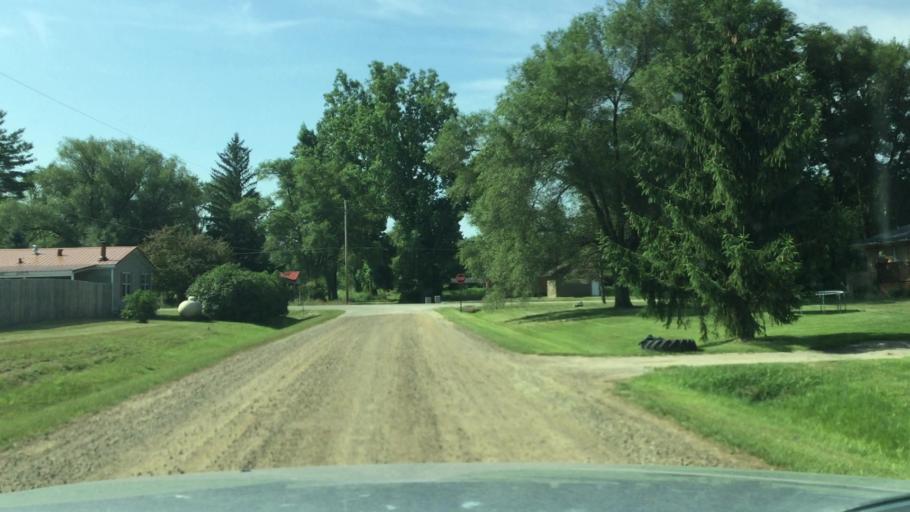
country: US
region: Michigan
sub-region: Genesee County
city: Montrose
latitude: 43.1342
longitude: -83.8427
